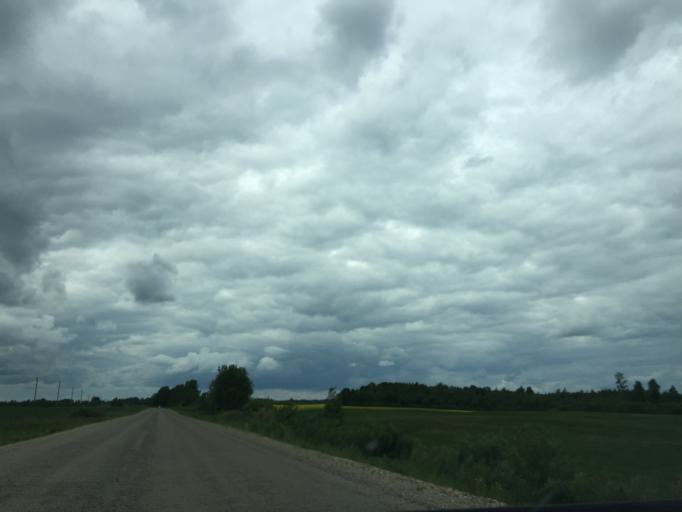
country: LV
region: Dagda
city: Dagda
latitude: 56.0382
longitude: 27.5894
